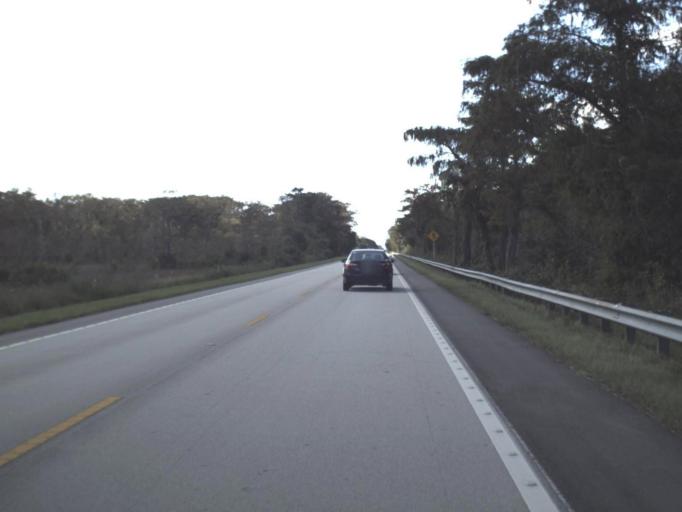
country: US
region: Florida
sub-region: Collier County
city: Lely Resort
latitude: 25.8684
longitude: -81.1469
